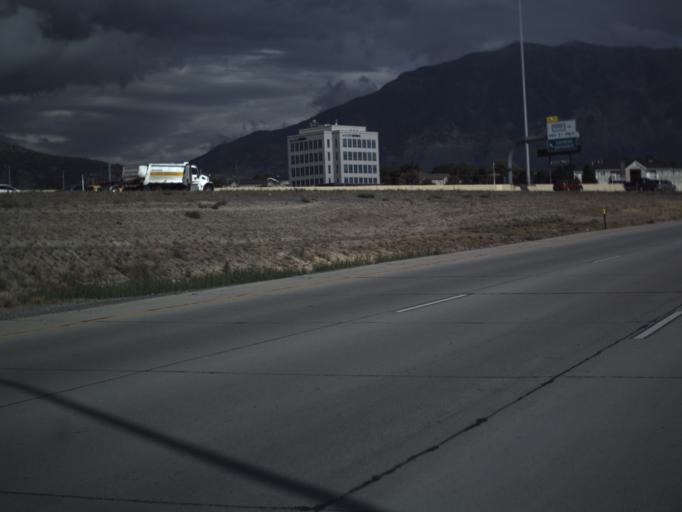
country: US
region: Utah
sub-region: Utah County
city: Lindon
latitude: 40.3254
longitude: -111.7325
